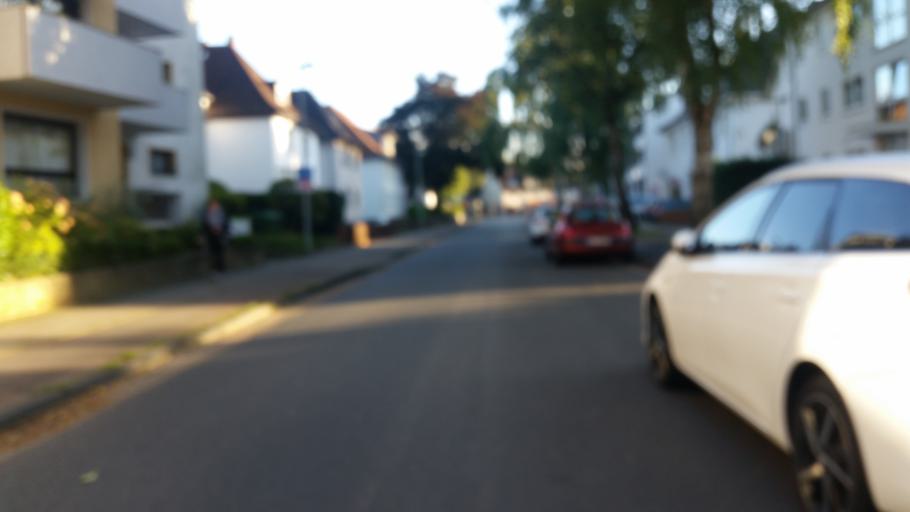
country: DE
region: Lower Saxony
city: Isernhagen Farster Bauerschaft
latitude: 52.3938
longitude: 9.8557
